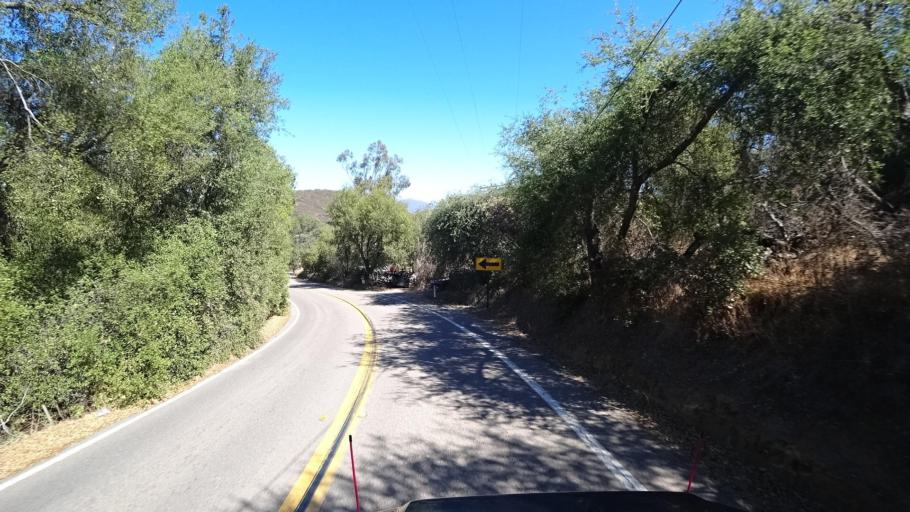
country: US
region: California
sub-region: San Diego County
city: Harbison Canyon
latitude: 32.7490
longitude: -116.7885
